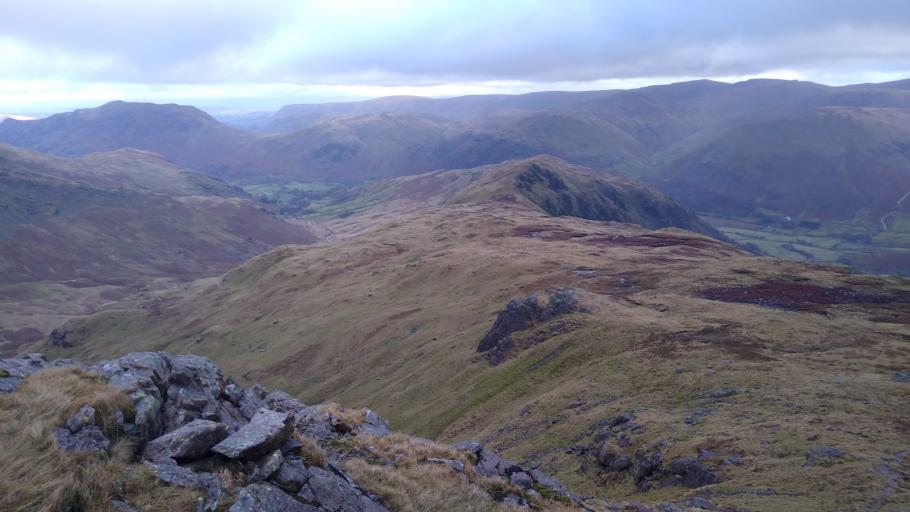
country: GB
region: England
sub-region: Cumbria
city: Ambleside
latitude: 54.4940
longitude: -2.9714
